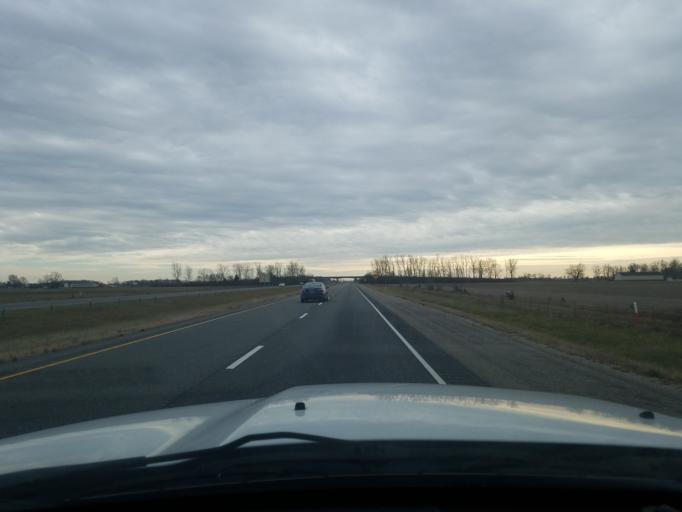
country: US
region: Indiana
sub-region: Grant County
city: Upland
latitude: 40.4057
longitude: -85.5492
